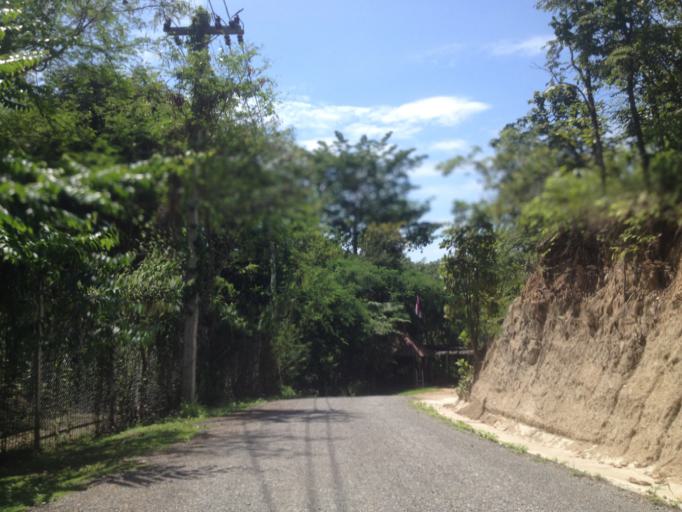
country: TH
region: Chiang Mai
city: Hang Dong
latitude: 18.7383
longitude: 98.9122
